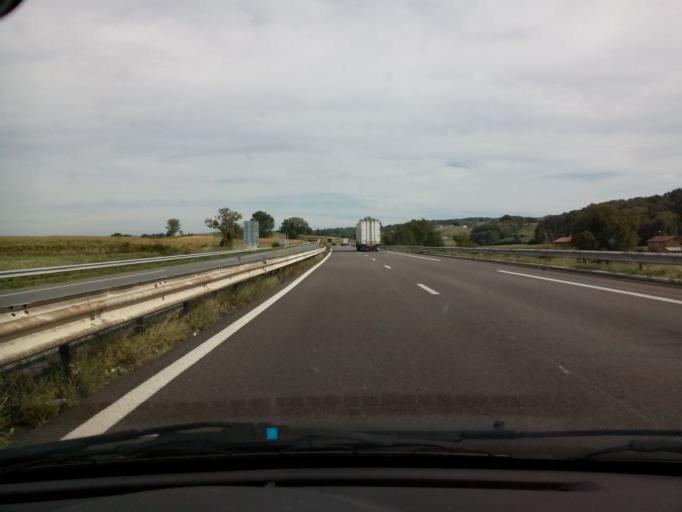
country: FR
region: Rhone-Alpes
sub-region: Departement de l'Isere
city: Cessieu
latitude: 45.5551
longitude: 5.3568
